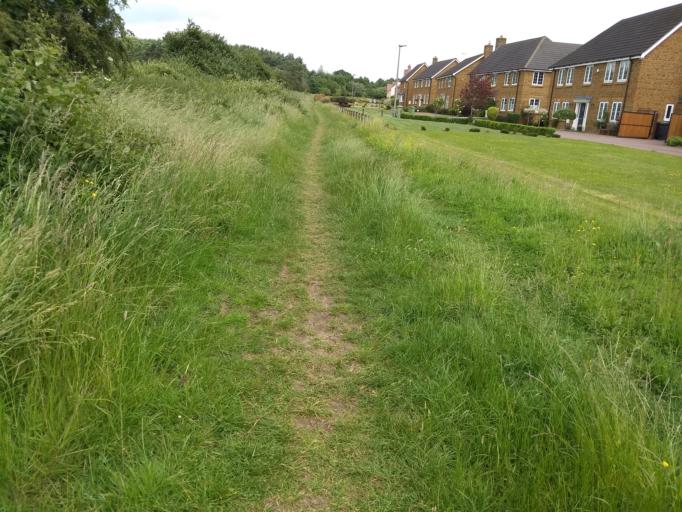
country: GB
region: England
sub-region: Milton Keynes
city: Shenley Church End
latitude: 52.0071
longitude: -0.8120
